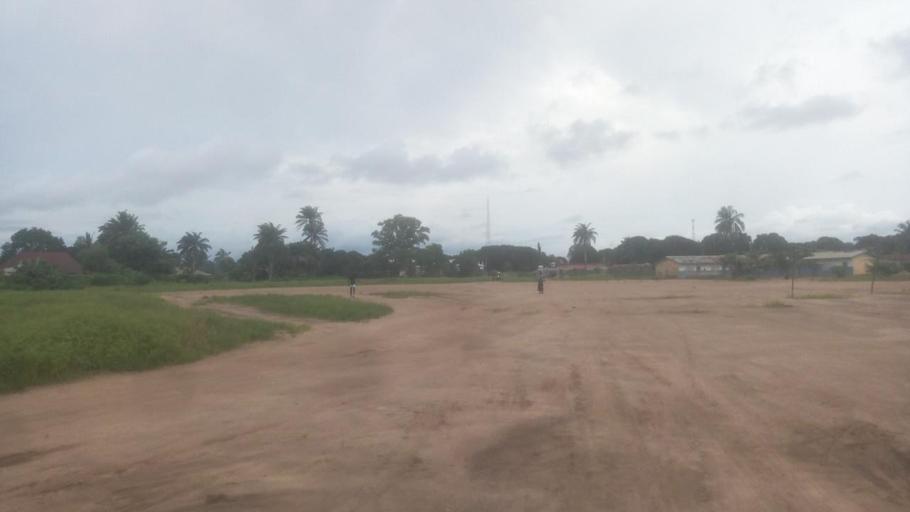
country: SL
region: Northern Province
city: Masoyila
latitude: 8.6082
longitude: -13.1868
